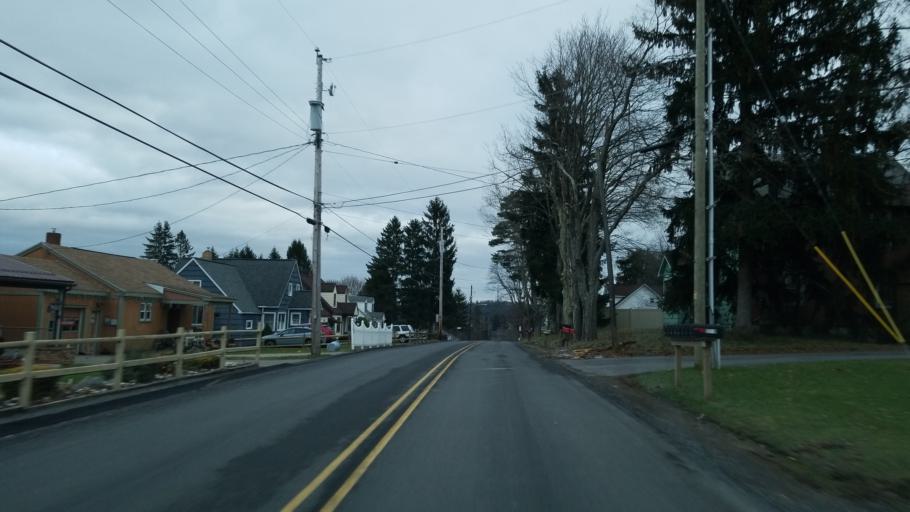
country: US
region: Pennsylvania
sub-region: Clearfield County
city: Sandy
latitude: 41.1127
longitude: -78.7836
